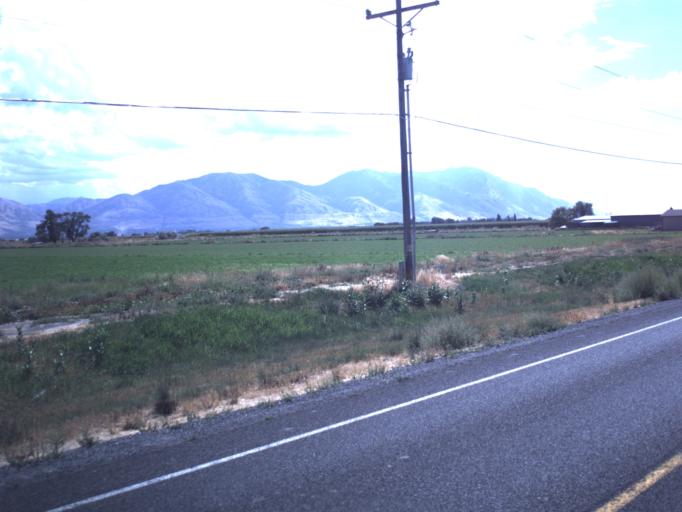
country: US
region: Utah
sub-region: Box Elder County
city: Honeyville
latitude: 41.5790
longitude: -112.1297
